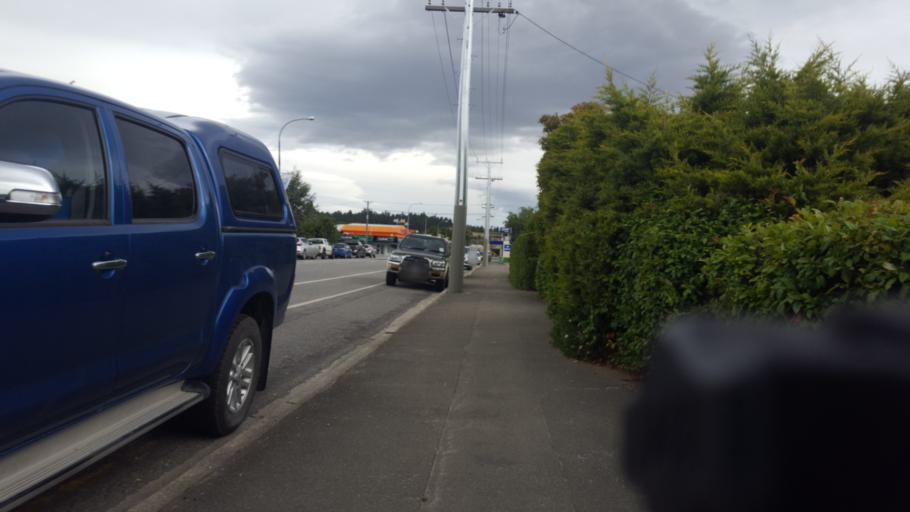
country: NZ
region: Otago
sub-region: Queenstown-Lakes District
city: Wanaka
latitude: -45.2543
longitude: 169.3940
